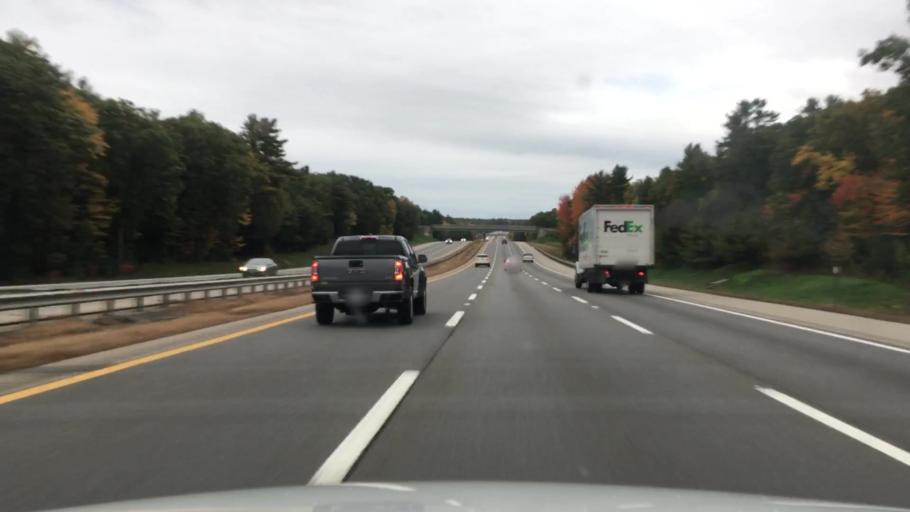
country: US
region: Maine
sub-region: York County
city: Ogunquit
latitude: 43.2758
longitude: -70.6182
